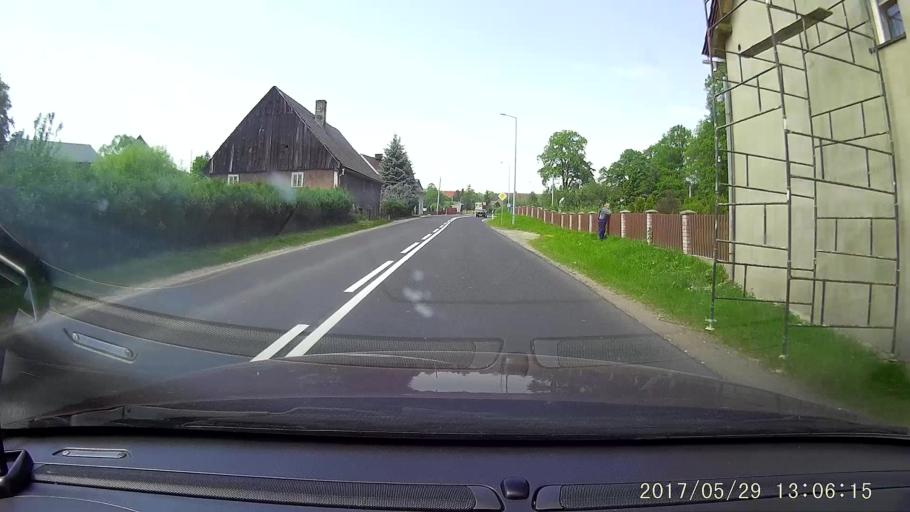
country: PL
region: Lower Silesian Voivodeship
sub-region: Powiat jeleniogorski
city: Stara Kamienica
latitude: 50.9500
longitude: 15.5828
